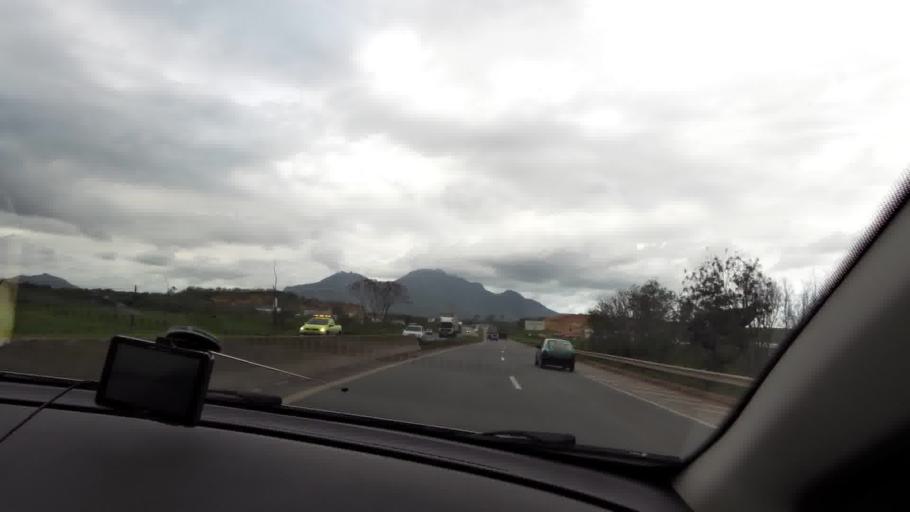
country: BR
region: Espirito Santo
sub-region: Vitoria
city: Vitoria
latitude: -20.2229
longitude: -40.3587
